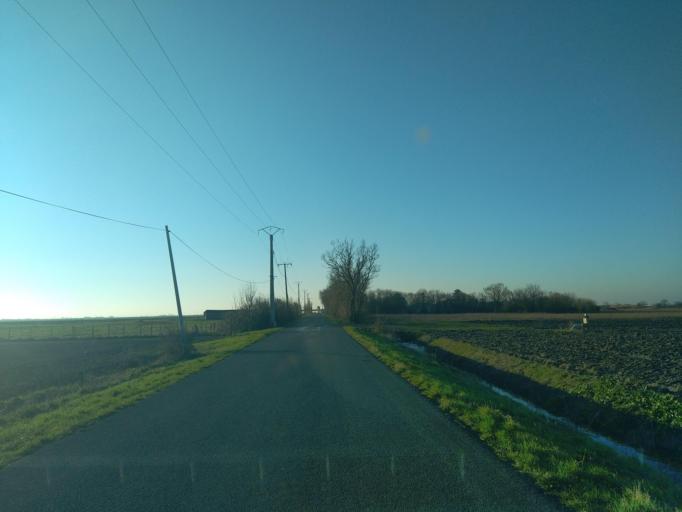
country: FR
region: Pays de la Loire
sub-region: Departement de la Vendee
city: Triaize
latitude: 46.3880
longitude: -1.2692
